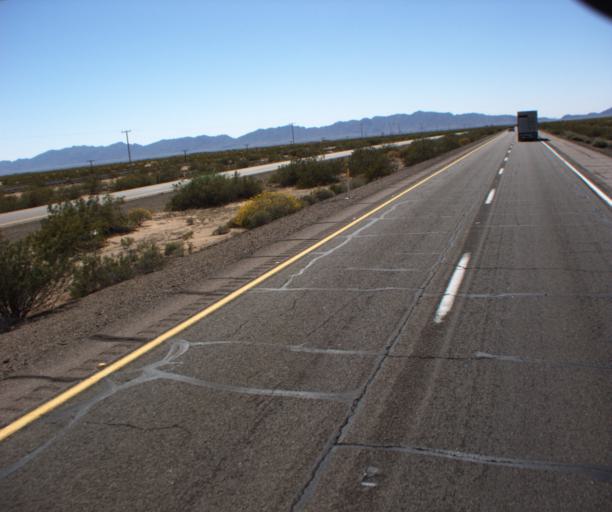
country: US
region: Arizona
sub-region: Yuma County
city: Wellton
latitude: 32.7824
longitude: -113.5789
